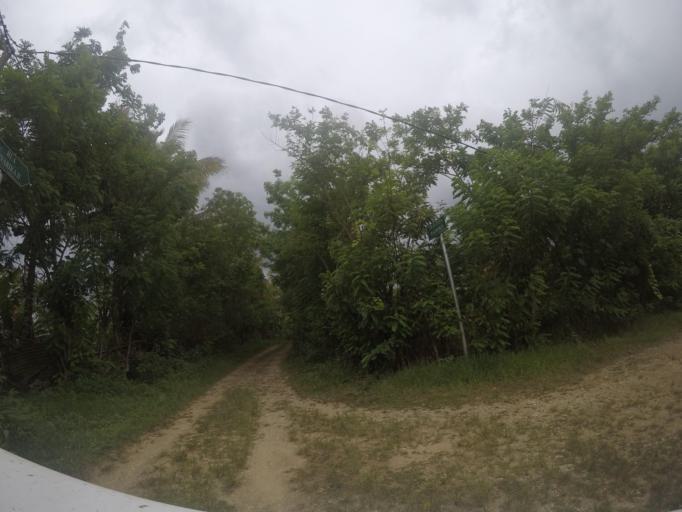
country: TL
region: Lautem
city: Lospalos
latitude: -8.5259
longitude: 126.9915
